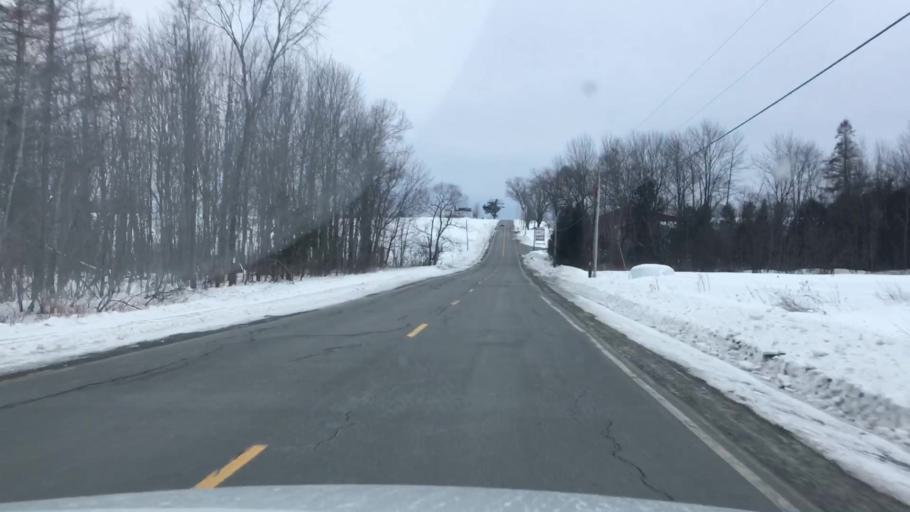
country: US
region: Maine
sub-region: Penobscot County
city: Garland
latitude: 44.9678
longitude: -69.1589
